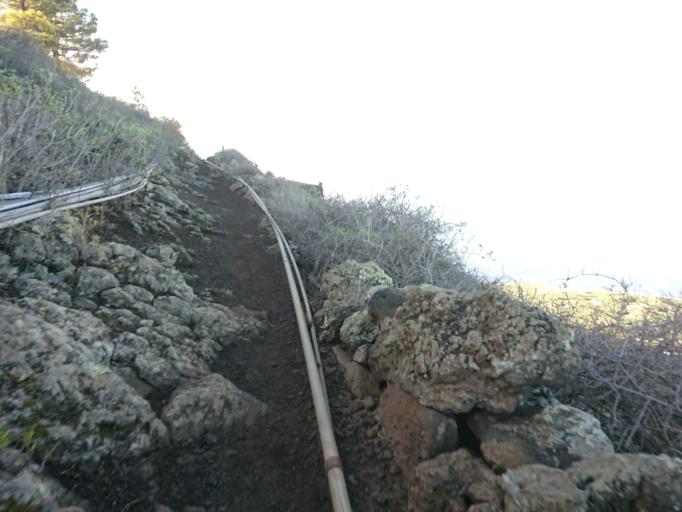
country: ES
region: Canary Islands
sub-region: Provincia de Santa Cruz de Tenerife
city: Los Llanos de Aridane
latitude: 28.6674
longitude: -17.9414
